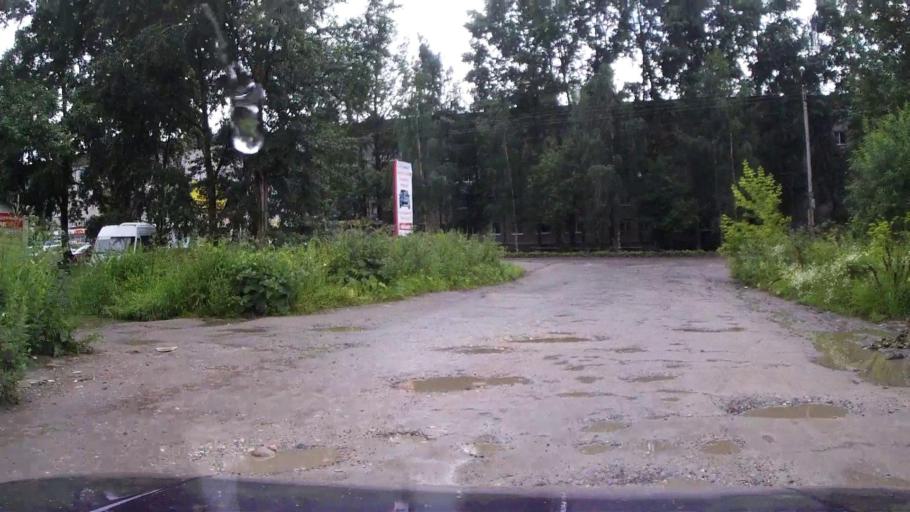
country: RU
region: Vologda
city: Vologda
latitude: 59.2076
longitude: 39.8617
